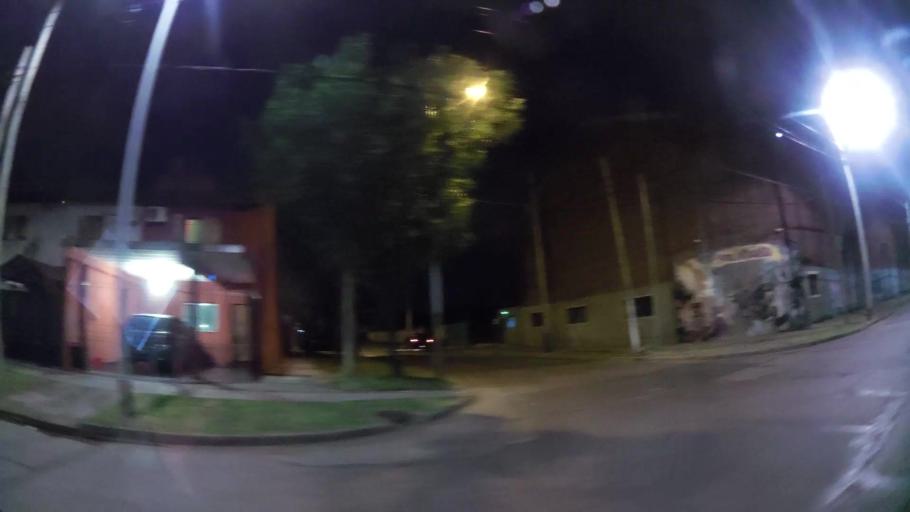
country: AR
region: Buenos Aires
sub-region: Partido de Lanus
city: Lanus
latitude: -34.7141
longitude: -58.3467
